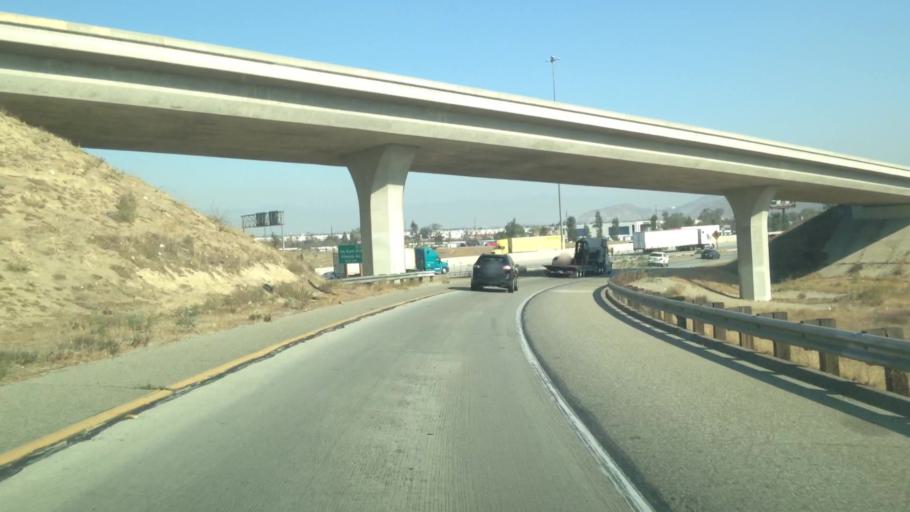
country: US
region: California
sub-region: Riverside County
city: Mira Loma
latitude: 34.0200
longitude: -117.5479
